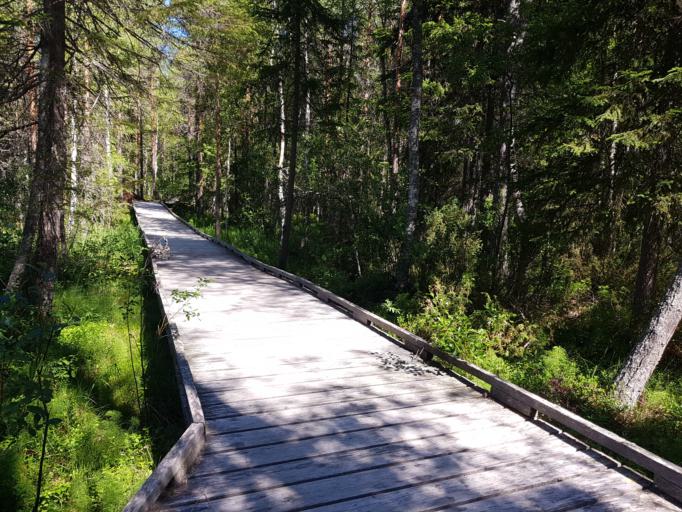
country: FI
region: Kainuu
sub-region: Kehys-Kainuu
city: Kuhmo
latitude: 64.1936
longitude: 29.5939
